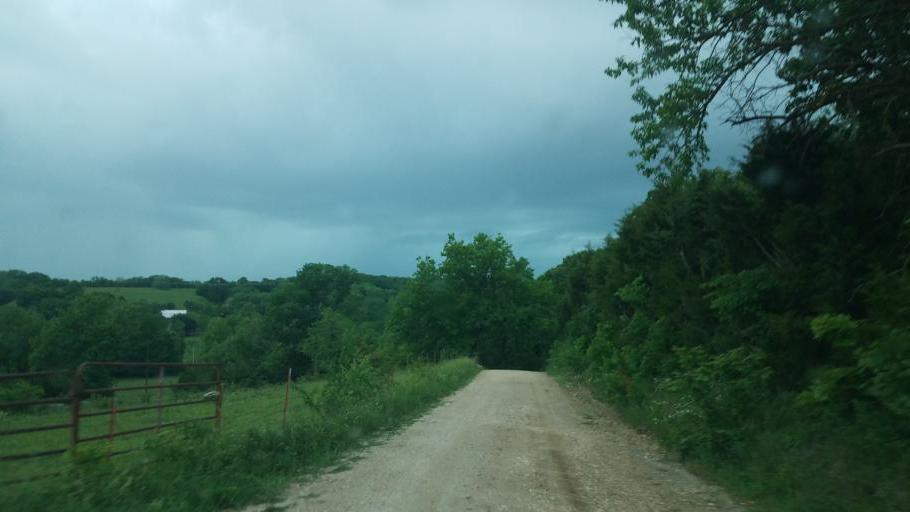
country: US
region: Missouri
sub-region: Moniteau County
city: California
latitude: 38.7503
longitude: -92.6259
